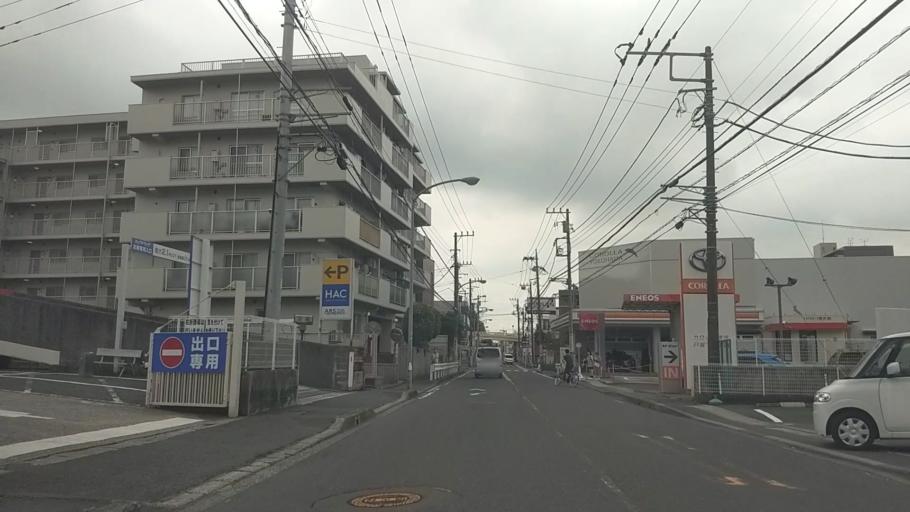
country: JP
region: Kanagawa
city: Kamakura
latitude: 35.3859
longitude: 139.5361
